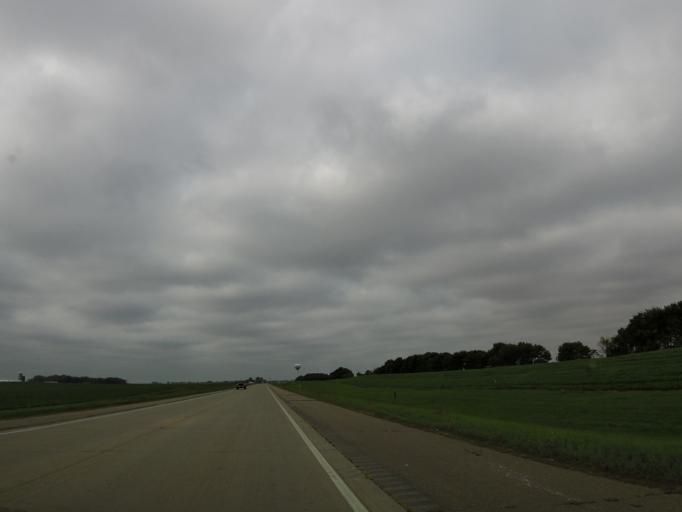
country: US
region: Minnesota
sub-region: Renville County
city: Renville
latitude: 44.7893
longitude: -95.1659
